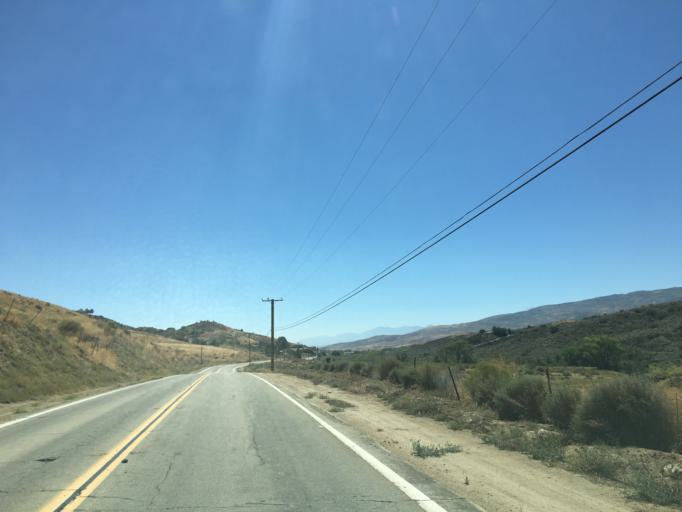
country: US
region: California
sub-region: Los Angeles County
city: Leona Valley
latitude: 34.6265
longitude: -118.3115
